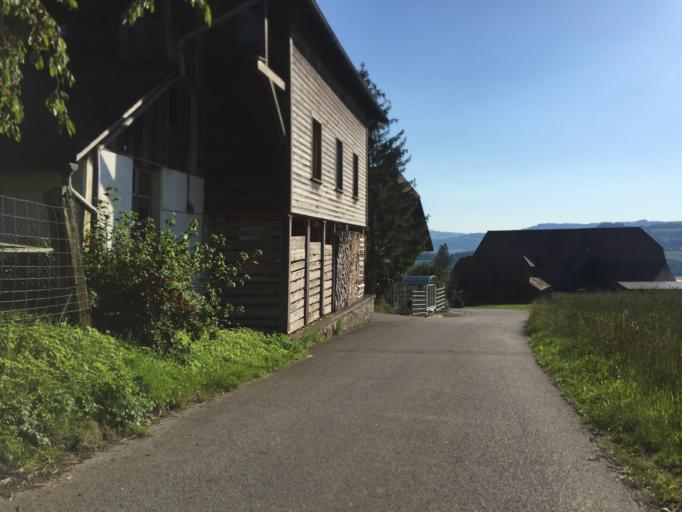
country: CH
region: Lucerne
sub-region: Entlebuch District
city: Oberdiessbach
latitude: 46.8441
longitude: 7.5977
